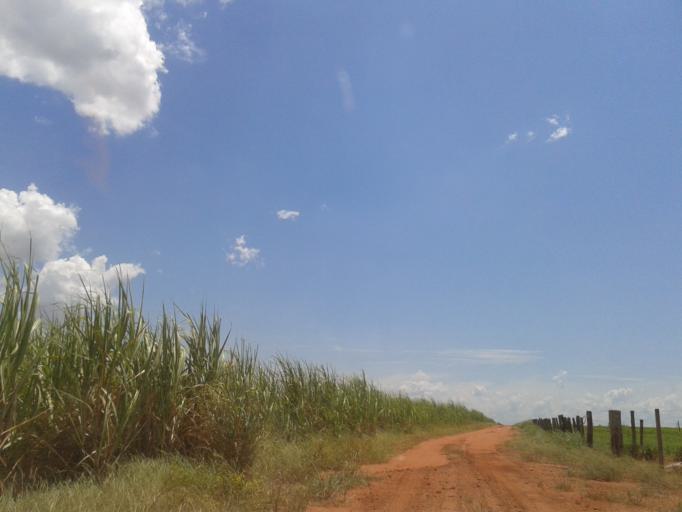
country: BR
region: Minas Gerais
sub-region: Santa Vitoria
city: Santa Vitoria
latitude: -19.1642
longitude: -50.4190
